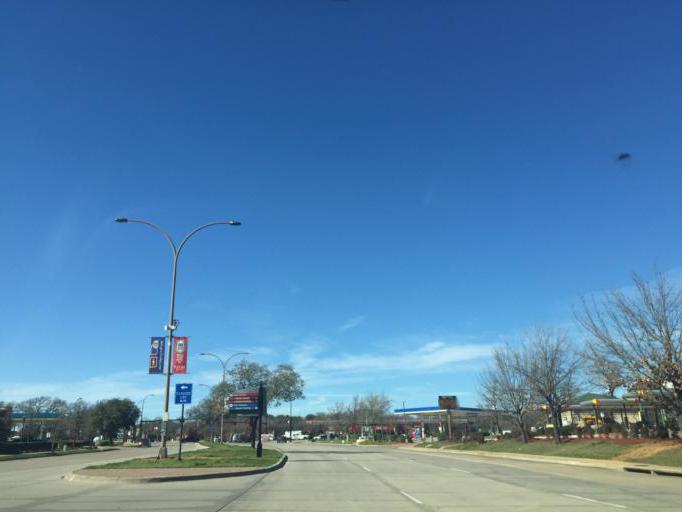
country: US
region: Texas
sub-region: Tarrant County
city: Arlington
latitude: 32.7621
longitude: -97.0737
